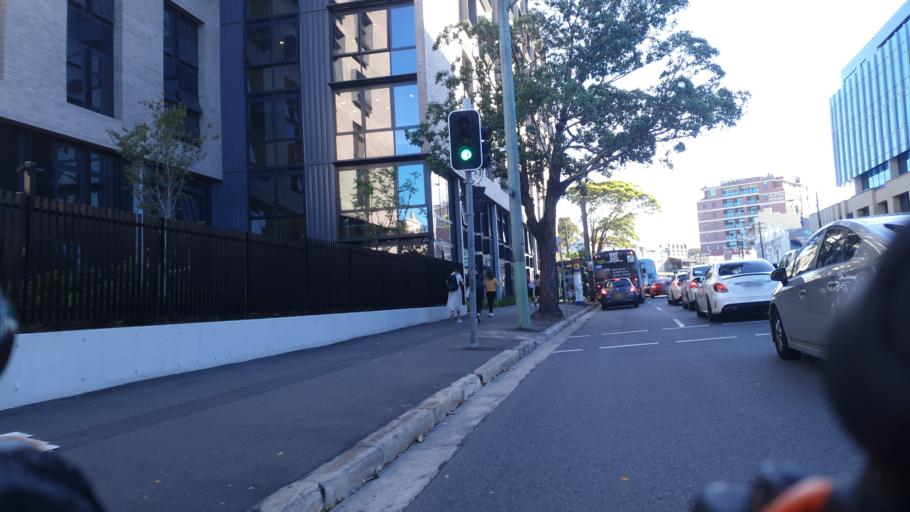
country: AU
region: New South Wales
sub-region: City of Sydney
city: Darlington
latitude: -33.8913
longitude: 151.1885
